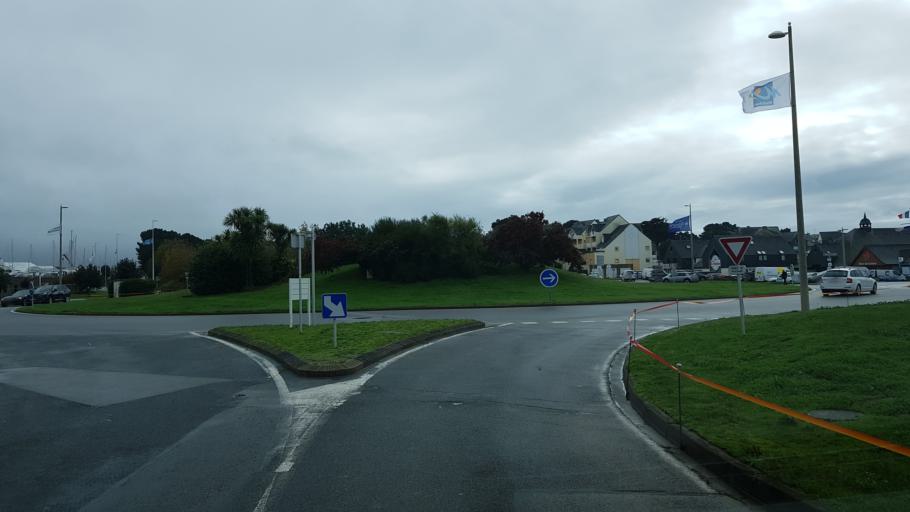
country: FR
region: Brittany
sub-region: Departement du Morbihan
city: Arzon
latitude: 47.5467
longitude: -2.8906
